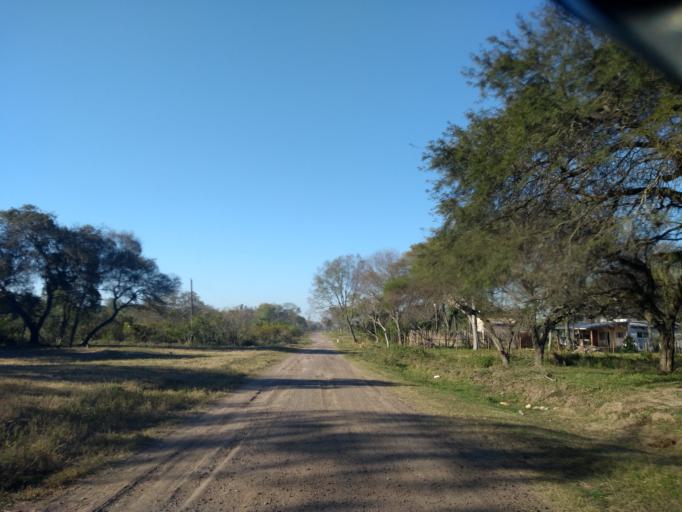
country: AR
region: Chaco
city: Barranqueras
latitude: -27.4380
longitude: -58.9291
